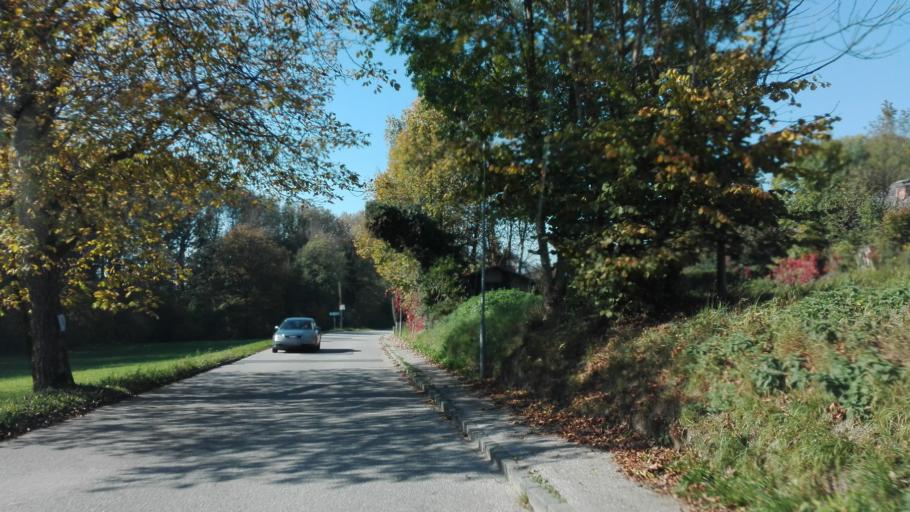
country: AT
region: Upper Austria
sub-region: Politischer Bezirk Urfahr-Umgebung
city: Ottensheim
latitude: 48.2963
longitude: 14.1725
